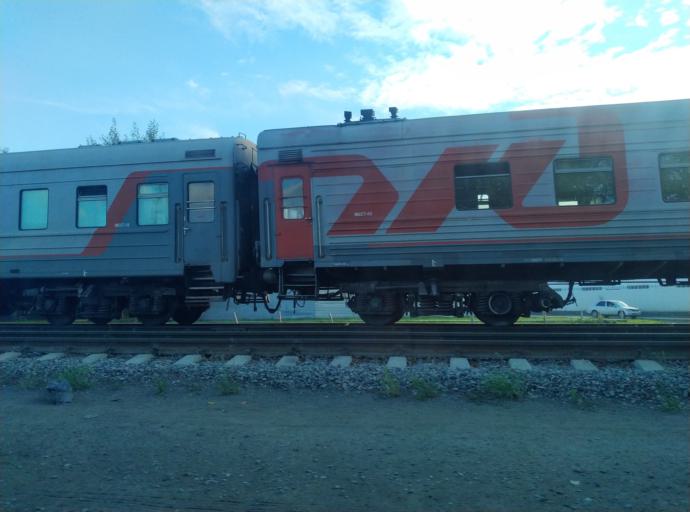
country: RU
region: Novosibirsk
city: Tolmachevo
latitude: 55.0146
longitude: 82.8070
